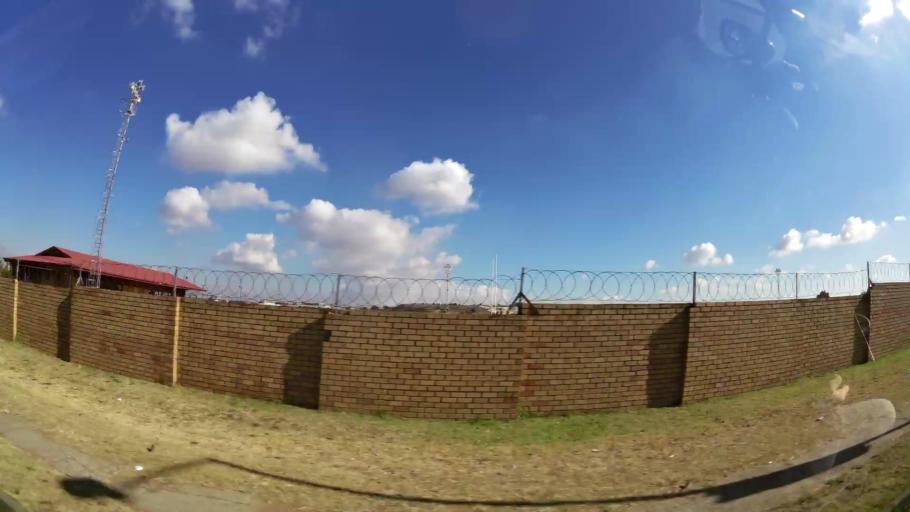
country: ZA
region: Gauteng
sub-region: City of Johannesburg Metropolitan Municipality
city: Roodepoort
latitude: -26.1483
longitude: 27.8232
